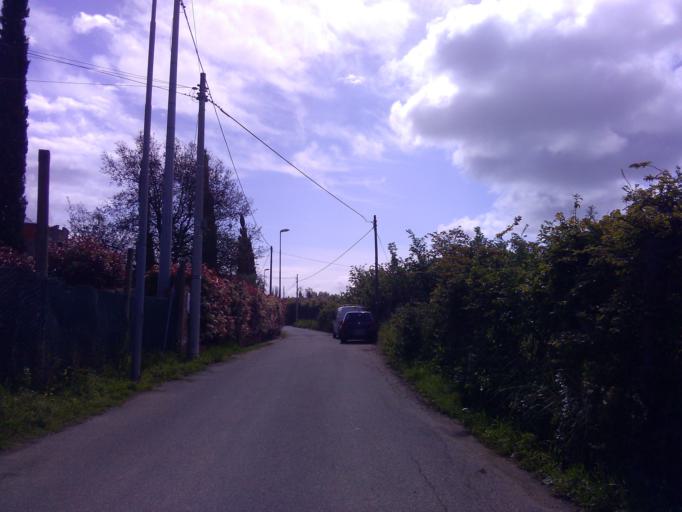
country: IT
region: Tuscany
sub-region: Provincia di Massa-Carrara
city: Marina di Carrara
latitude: 44.0482
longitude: 10.0378
